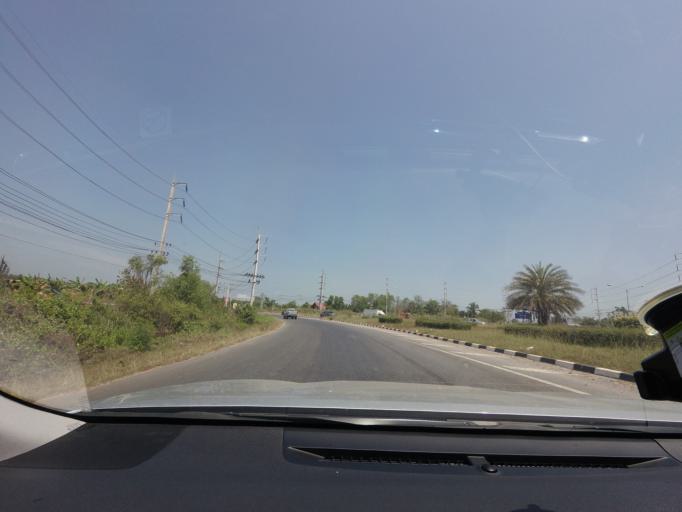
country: TH
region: Surat Thani
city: Surat Thani
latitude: 9.1637
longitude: 99.3717
